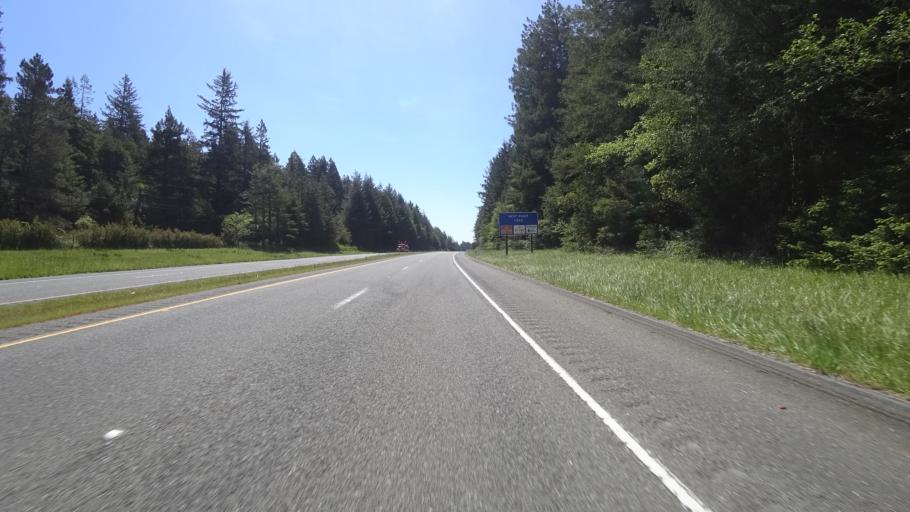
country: US
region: California
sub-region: Humboldt County
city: Westhaven-Moonstone
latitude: 41.0728
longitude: -124.1414
